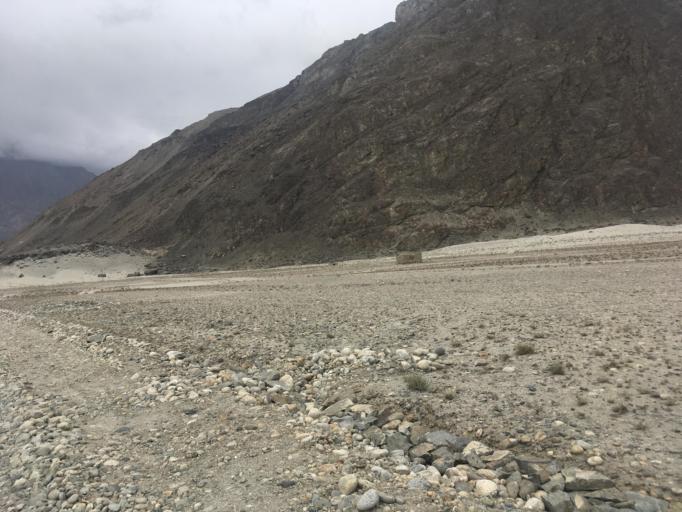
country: PK
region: Gilgit-Baltistan
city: Skardu
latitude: 35.3119
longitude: 75.6581
